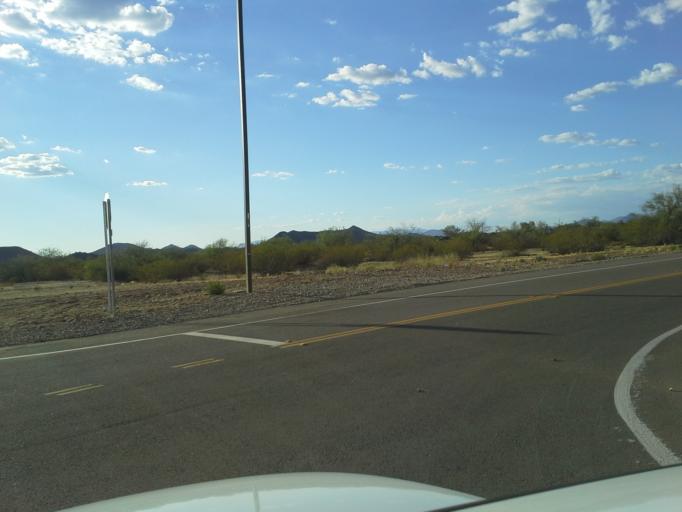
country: US
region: Arizona
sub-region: Maricopa County
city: Cave Creek
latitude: 33.6823
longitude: -112.0086
